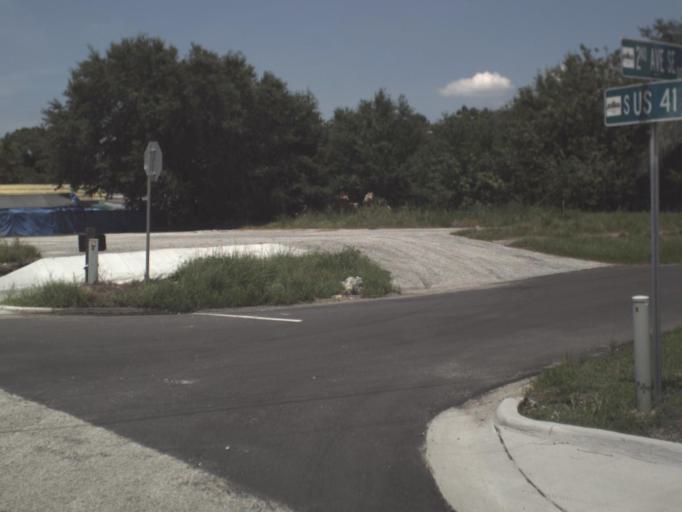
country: US
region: Florida
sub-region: Hillsborough County
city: Ruskin
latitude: 27.7177
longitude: -82.4340
